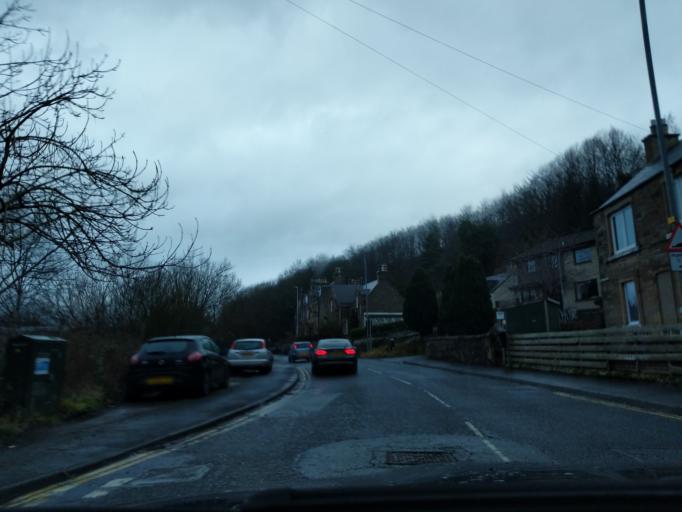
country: GB
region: Scotland
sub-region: The Scottish Borders
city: Galashiels
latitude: 55.6246
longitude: -2.8217
